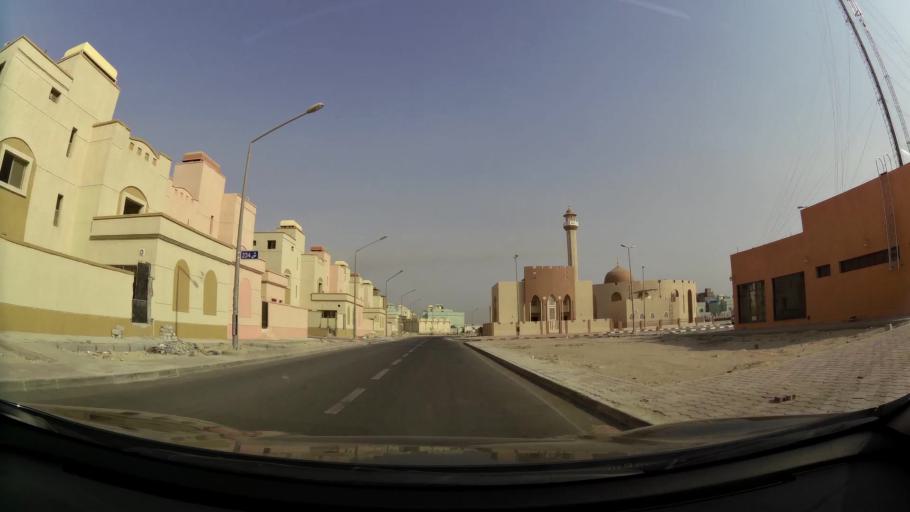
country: KW
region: Al Asimah
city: Ar Rabiyah
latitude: 29.3319
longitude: 47.8028
